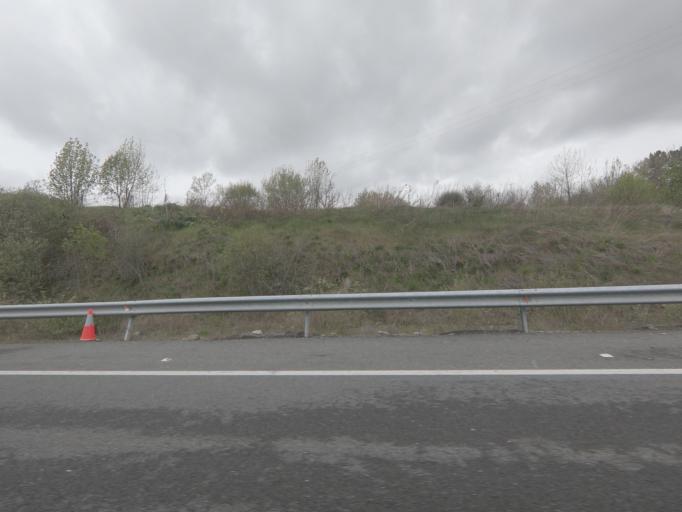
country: ES
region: Castille and Leon
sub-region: Provincia de Salamanca
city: Puerto de Bejar
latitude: 40.3513
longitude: -5.8430
